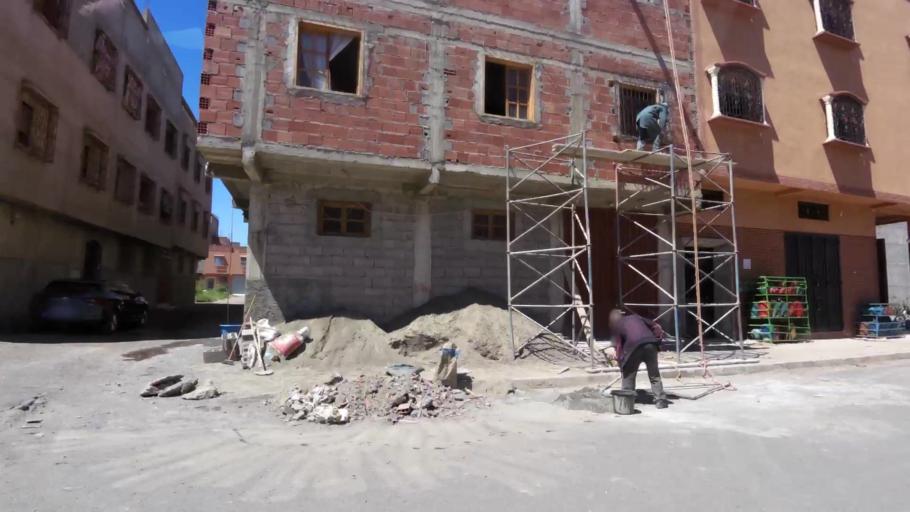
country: MA
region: Marrakech-Tensift-Al Haouz
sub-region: Marrakech
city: Marrakesh
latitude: 31.5512
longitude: -7.9779
